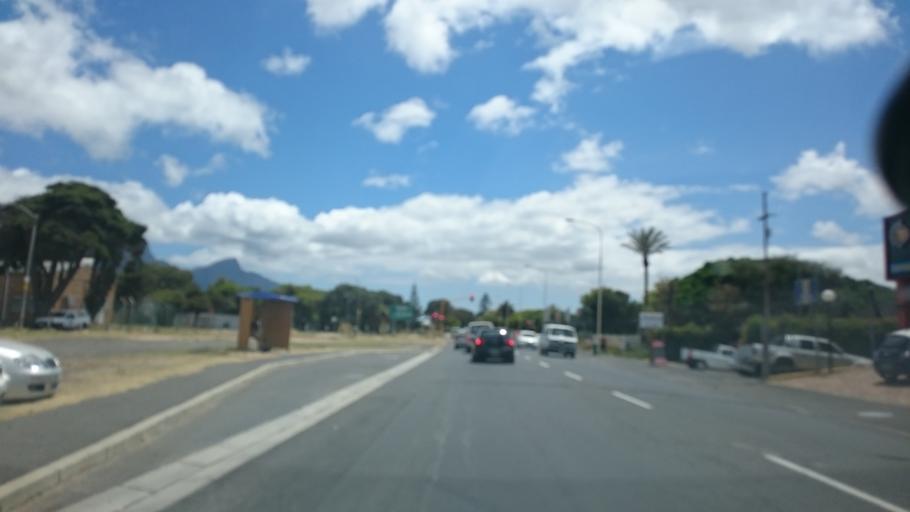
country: ZA
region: Western Cape
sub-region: City of Cape Town
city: Bergvliet
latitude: -34.0516
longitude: 18.4617
